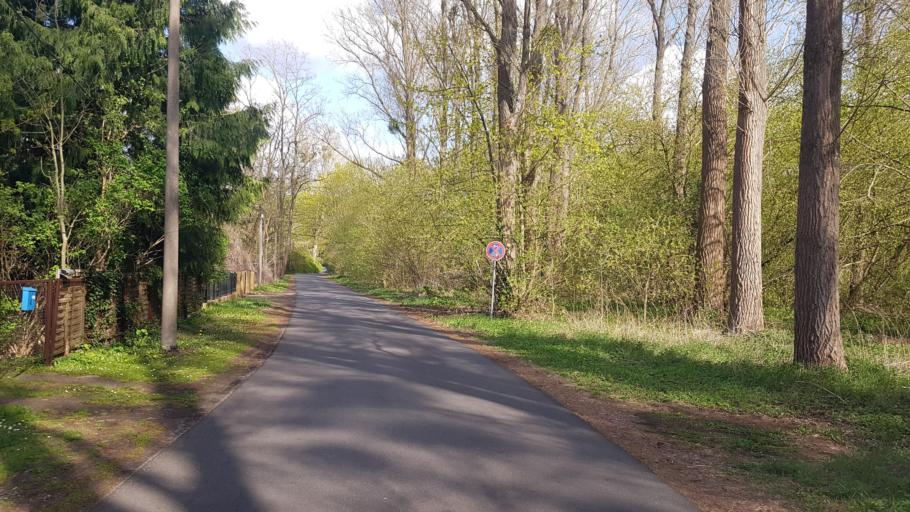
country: DE
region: Brandenburg
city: Luckenwalde
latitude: 52.0750
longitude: 13.1608
